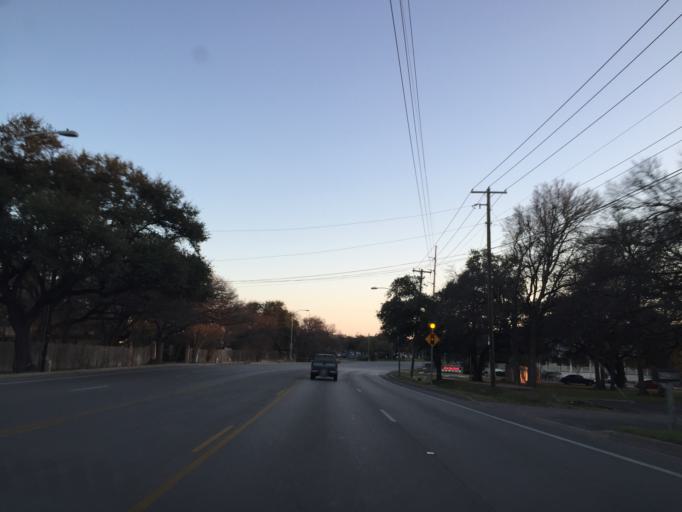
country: US
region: Texas
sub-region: Williamson County
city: Jollyville
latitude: 30.4109
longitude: -97.7478
